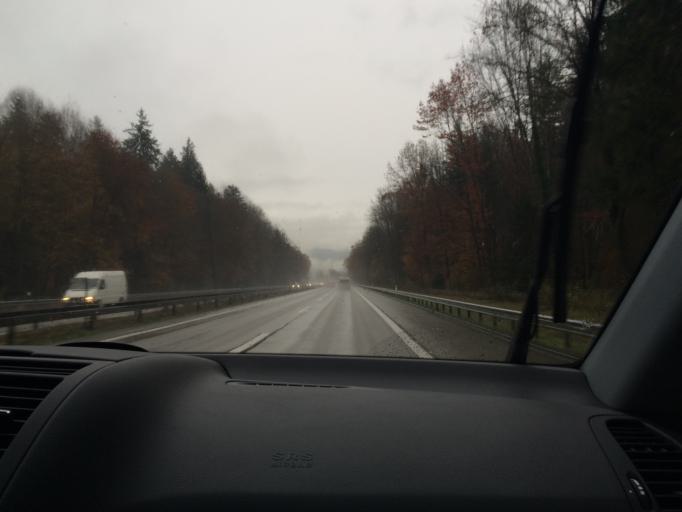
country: CH
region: Solothurn
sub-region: Bezirk Wasseramt
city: Kriegstetten
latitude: 47.1828
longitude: 7.5949
